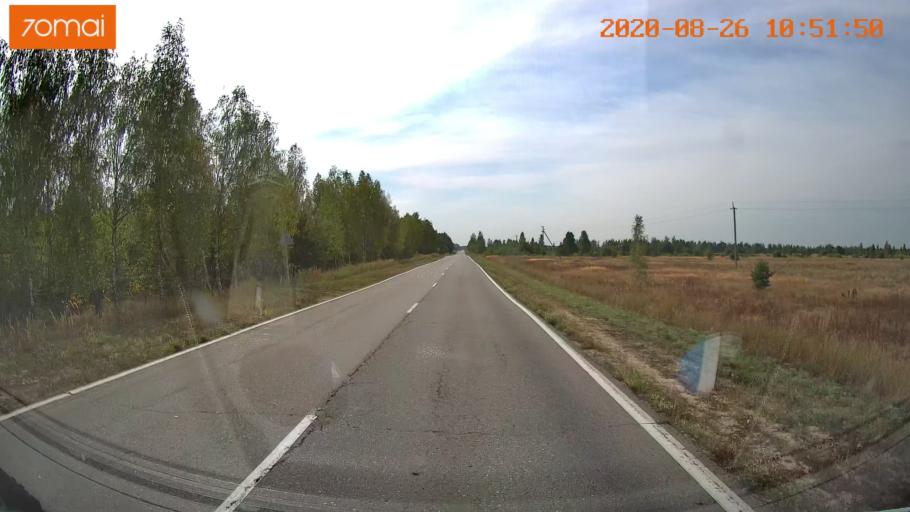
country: RU
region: Rjazan
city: Lashma
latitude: 54.6662
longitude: 41.1544
